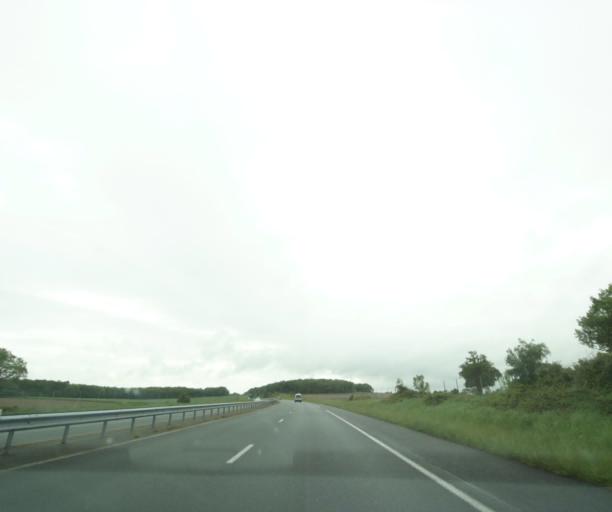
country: FR
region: Poitou-Charentes
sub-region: Departement de la Charente-Maritime
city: Chermignac
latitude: 45.7143
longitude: -0.6699
